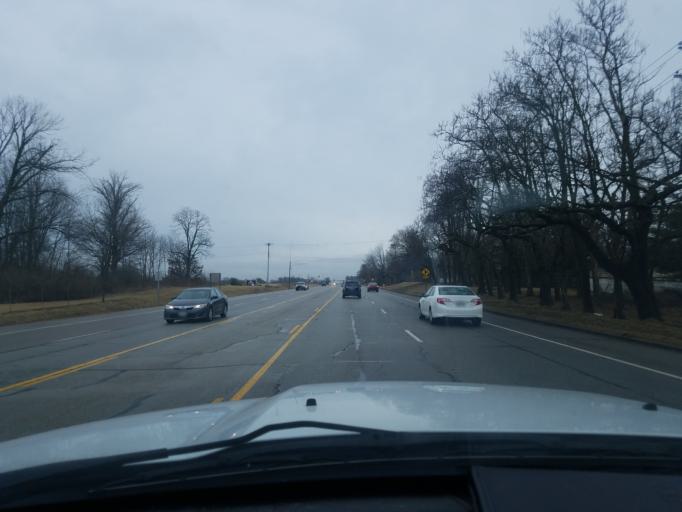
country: US
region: Ohio
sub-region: Butler County
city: Wetherington
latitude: 39.3525
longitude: -84.3563
